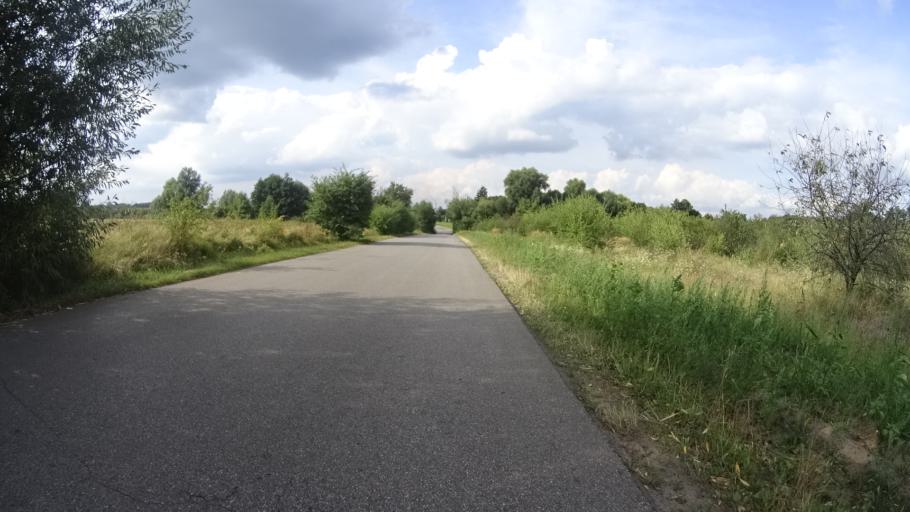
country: PL
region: Masovian Voivodeship
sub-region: Powiat grojecki
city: Mogielnica
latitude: 51.6628
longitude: 20.7452
